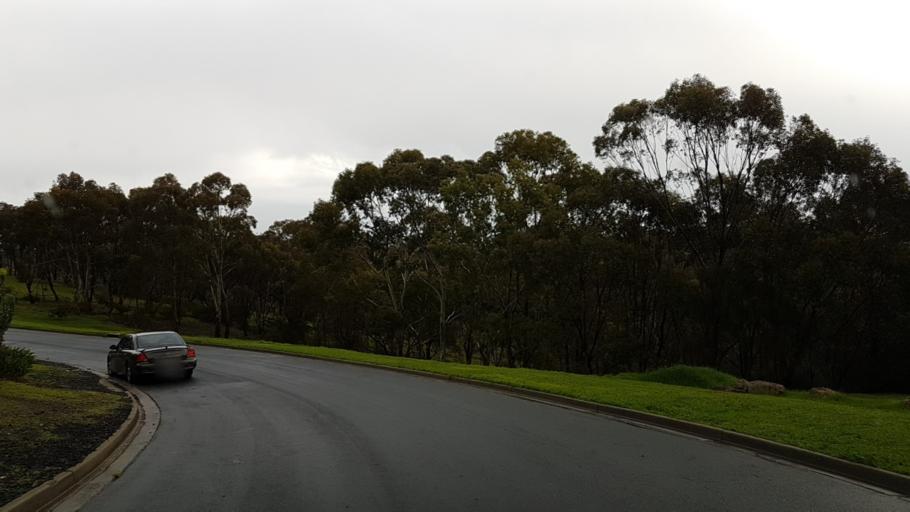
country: AU
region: South Australia
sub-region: Onkaparinga
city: Bedford Park
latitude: -35.0439
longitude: 138.5780
